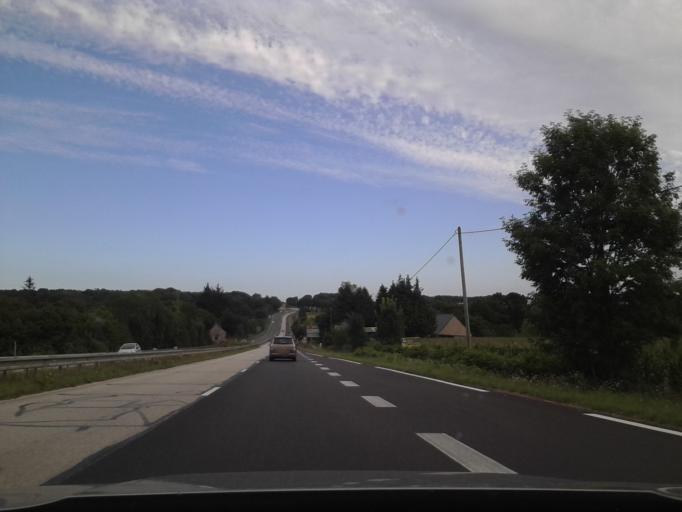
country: FR
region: Lower Normandy
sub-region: Departement de la Manche
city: Brix
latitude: 49.5590
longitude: -1.5662
